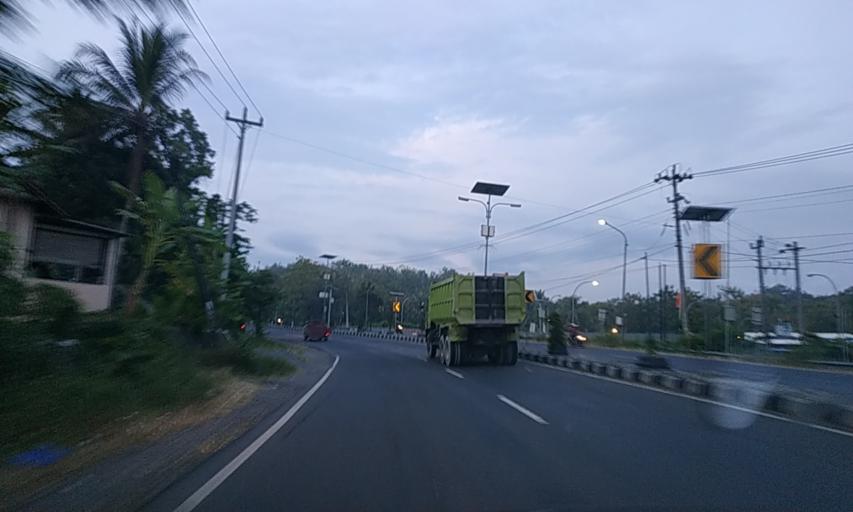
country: ID
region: Daerah Istimewa Yogyakarta
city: Srandakan
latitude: -7.8558
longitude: 110.2152
